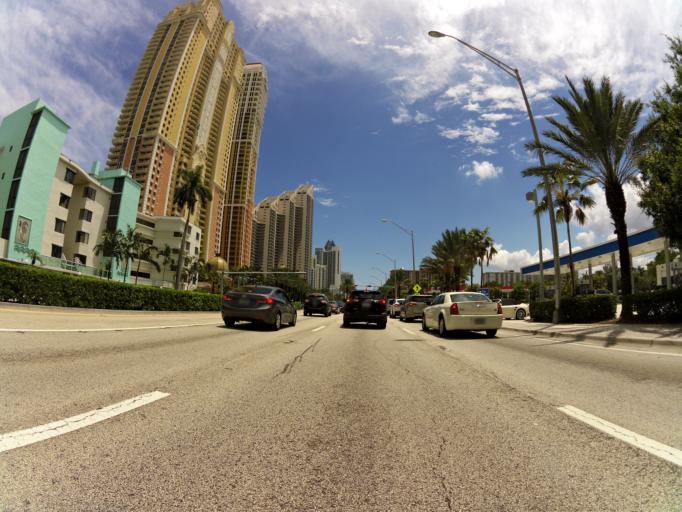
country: US
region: Florida
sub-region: Miami-Dade County
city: Sunny Isles Beach
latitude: 25.9420
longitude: -80.1213
